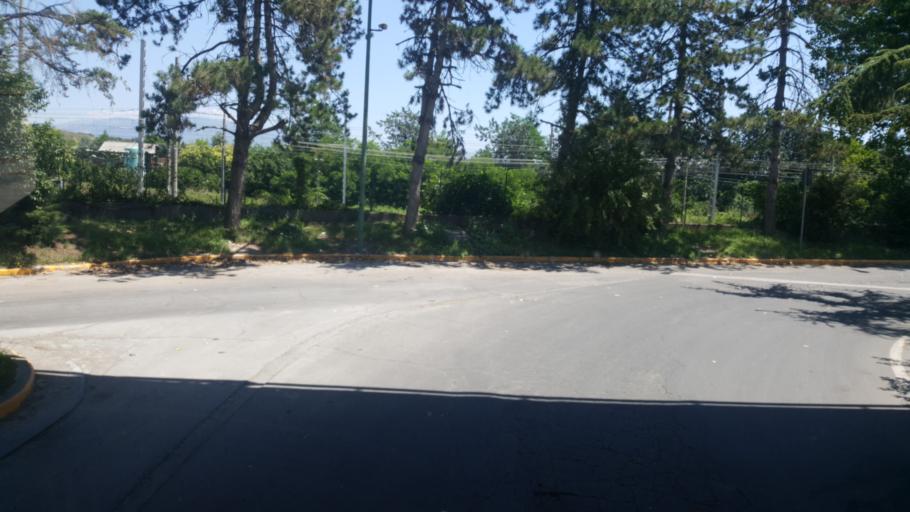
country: IT
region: Latium
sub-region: Citta metropolitana di Roma Capitale
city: Colleferro
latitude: 41.7363
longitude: 13.0068
